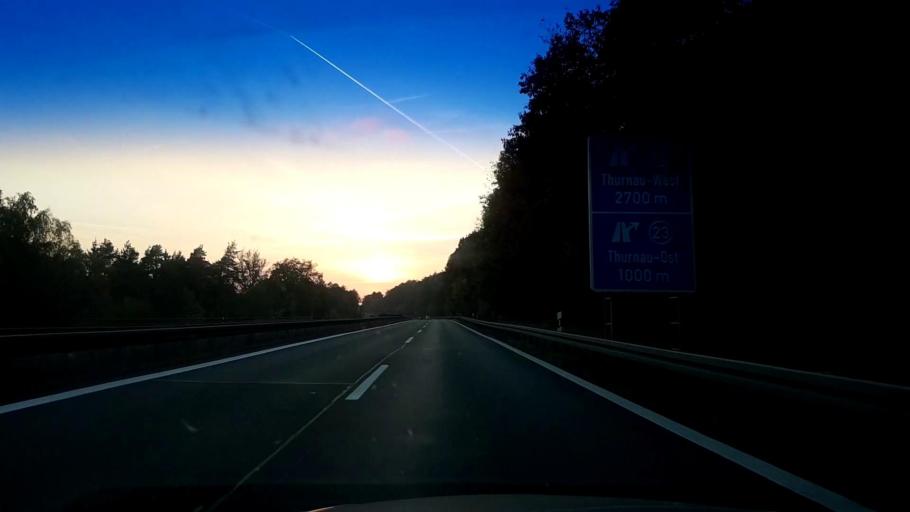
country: DE
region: Bavaria
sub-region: Upper Franconia
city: Eckersdorf
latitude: 50.0238
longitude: 11.4299
